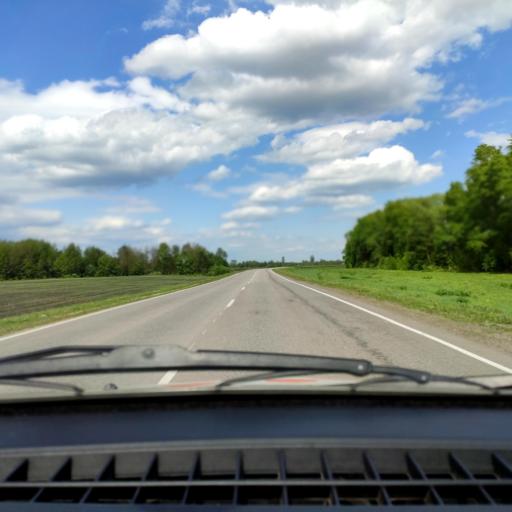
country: RU
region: Bashkortostan
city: Krasnaya Gorka
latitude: 55.0422
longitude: 56.5131
